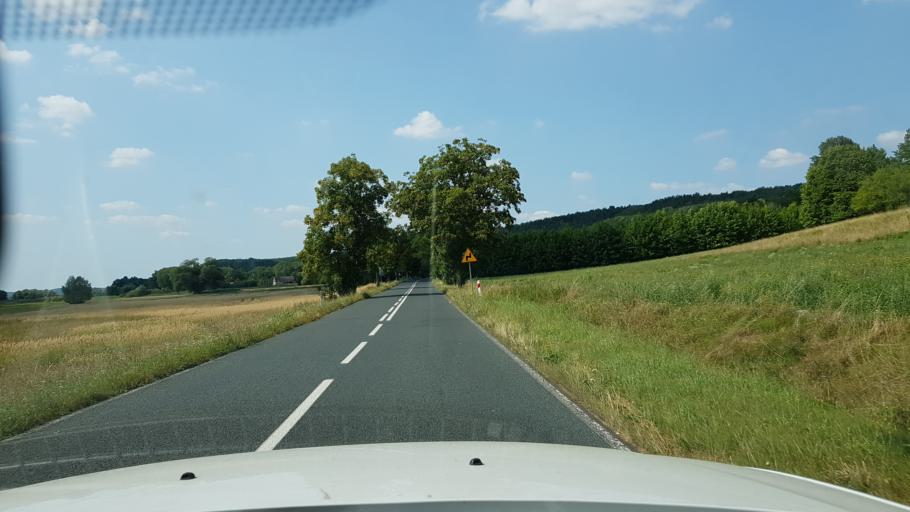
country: PL
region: West Pomeranian Voivodeship
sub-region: Powiat gryfinski
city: Cedynia
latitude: 52.8327
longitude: 14.2067
